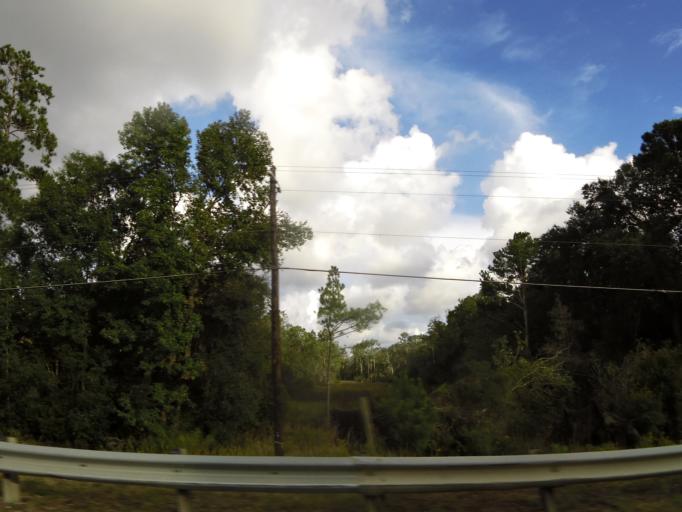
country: US
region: Georgia
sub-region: Liberty County
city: Midway
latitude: 31.7719
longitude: -81.4469
